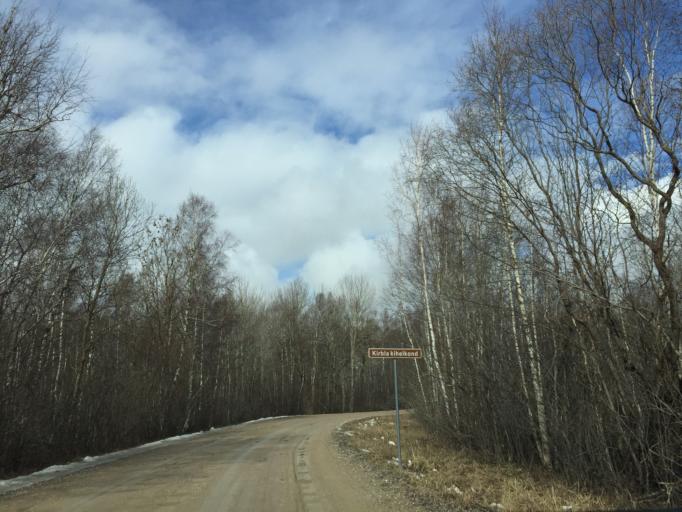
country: EE
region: Laeaene
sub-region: Lihula vald
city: Lihula
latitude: 58.7266
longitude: 23.8297
